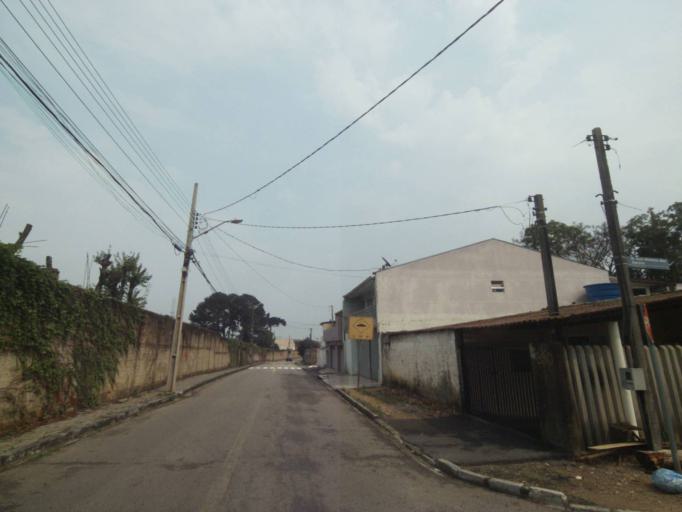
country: BR
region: Parana
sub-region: Curitiba
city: Curitiba
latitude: -25.4827
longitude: -49.2994
